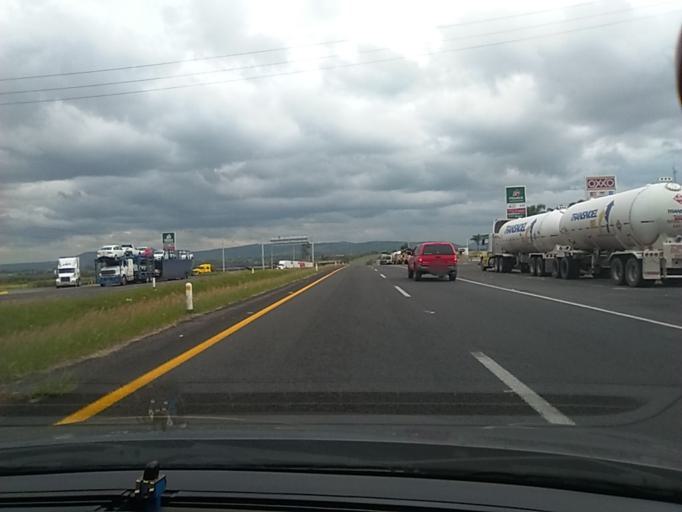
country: MX
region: Jalisco
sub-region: Tonala
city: Mismaloya (Fraccionamiento Pedregal de Santa Martha)
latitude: 20.6048
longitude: -103.1294
